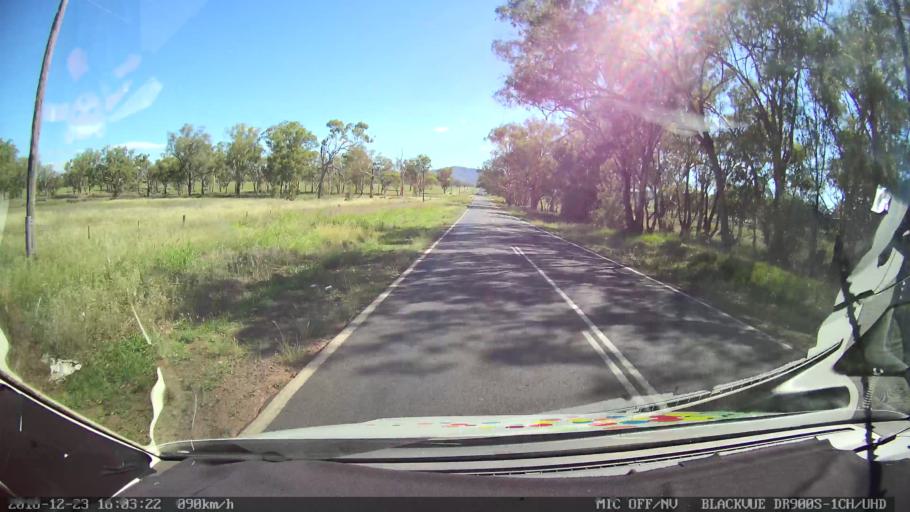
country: AU
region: New South Wales
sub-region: Tamworth Municipality
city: Phillip
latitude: -31.2427
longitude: 150.8012
